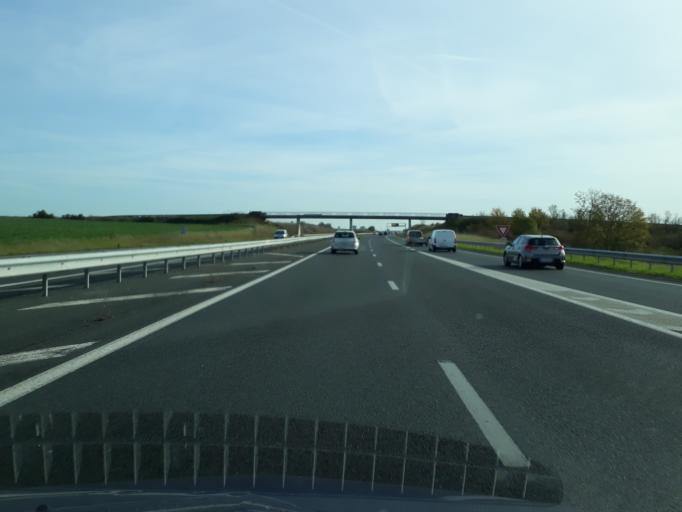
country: FR
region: Bourgogne
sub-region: Departement de l'Yonne
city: Thorigny-sur-Oreuse
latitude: 48.2447
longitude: 3.5611
